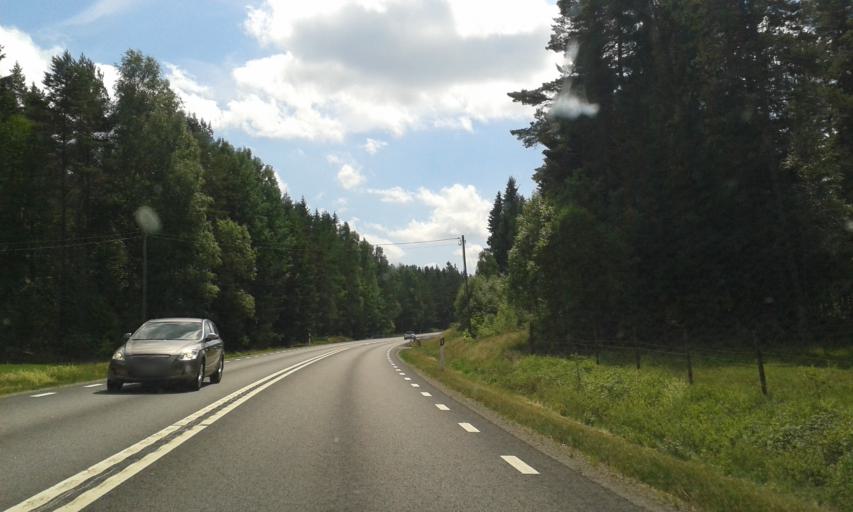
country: SE
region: Joenkoeping
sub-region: Varnamo Kommun
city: Rydaholm
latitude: 56.9234
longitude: 14.4180
